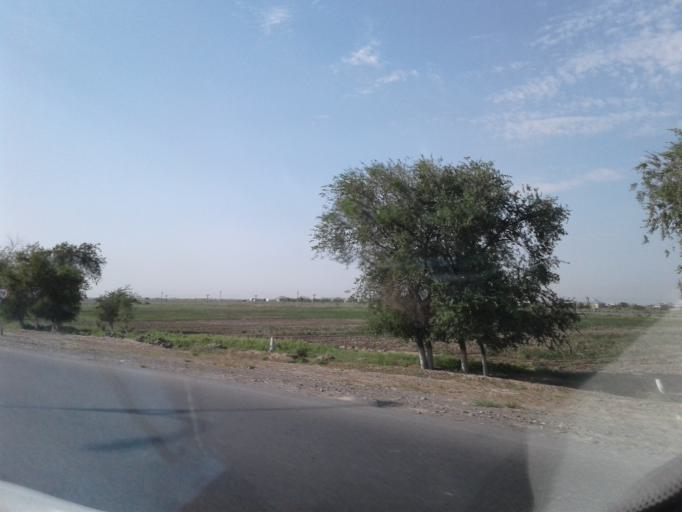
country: TM
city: Murgab
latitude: 37.5174
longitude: 61.9233
